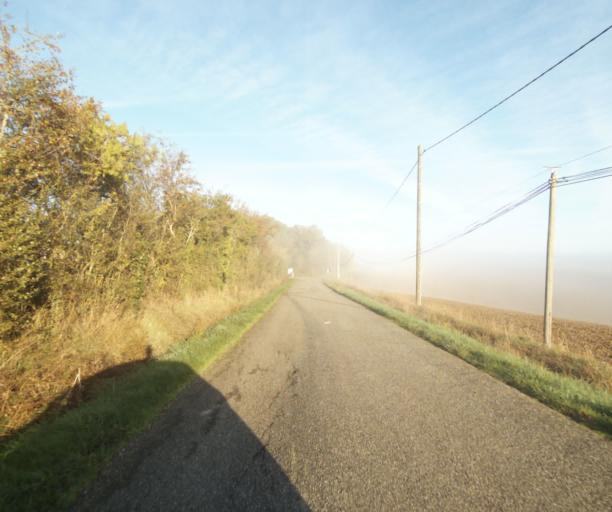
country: FR
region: Midi-Pyrenees
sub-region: Departement de la Haute-Garonne
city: Villemur-sur-Tarn
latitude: 43.9175
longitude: 1.4938
